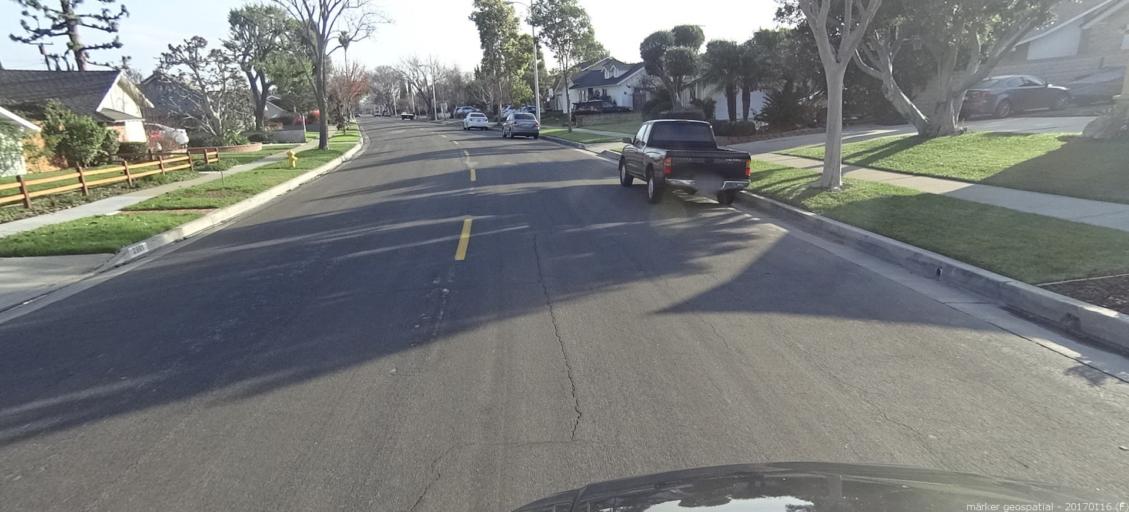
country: US
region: California
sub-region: Orange County
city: Rossmoor
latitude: 33.7886
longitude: -118.0825
